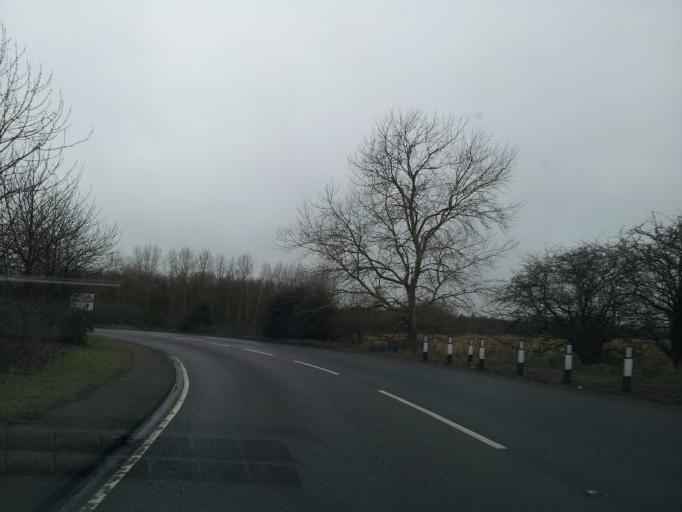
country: GB
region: England
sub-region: Essex
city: Manningtree
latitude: 51.9521
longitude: 1.0501
